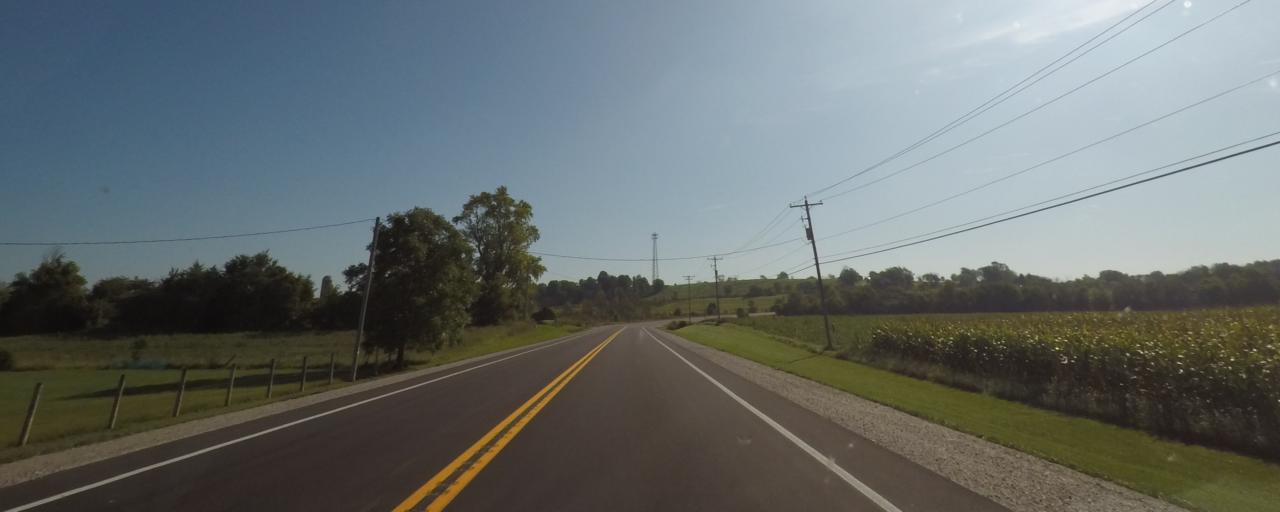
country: US
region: Wisconsin
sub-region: Jefferson County
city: Johnson Creek
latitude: 43.0193
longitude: -88.7175
